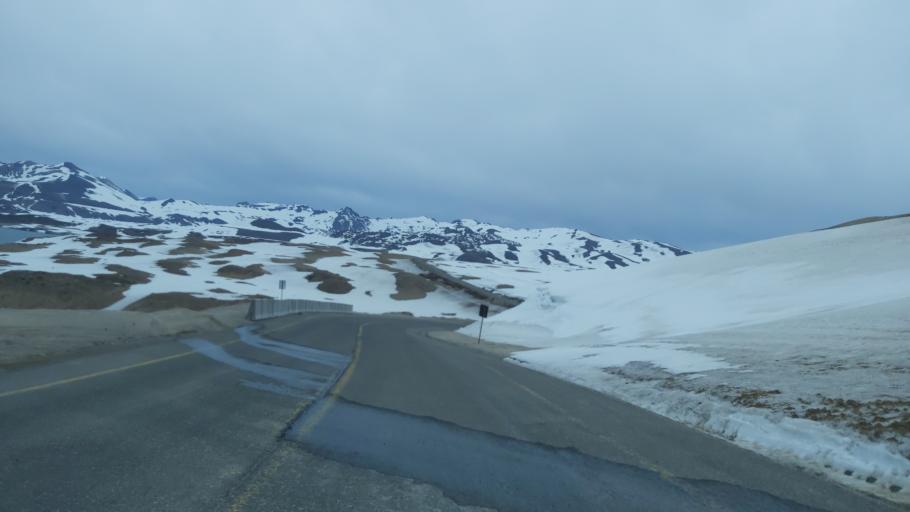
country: CL
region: Maule
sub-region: Provincia de Linares
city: Colbun
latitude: -36.0190
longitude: -70.5221
